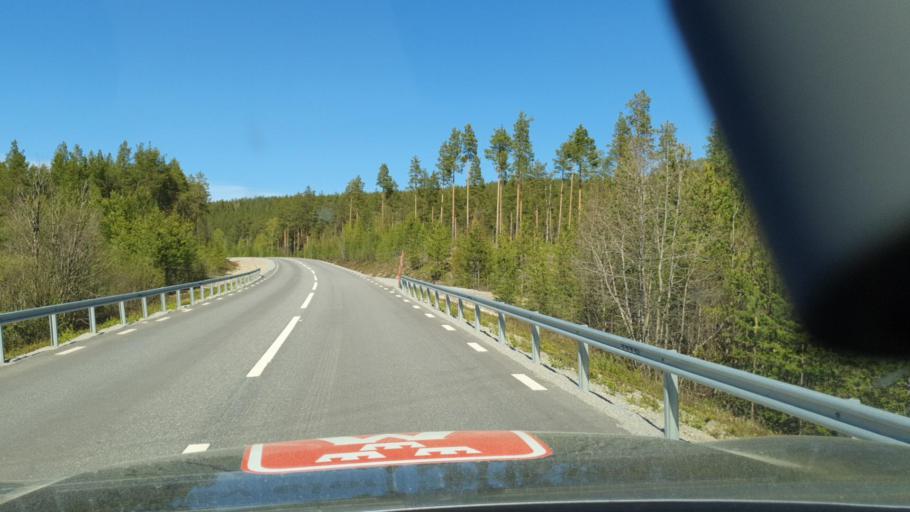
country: SE
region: Vaesternorrland
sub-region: OErnskoeldsviks Kommun
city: Bredbyn
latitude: 63.9293
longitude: 18.4827
